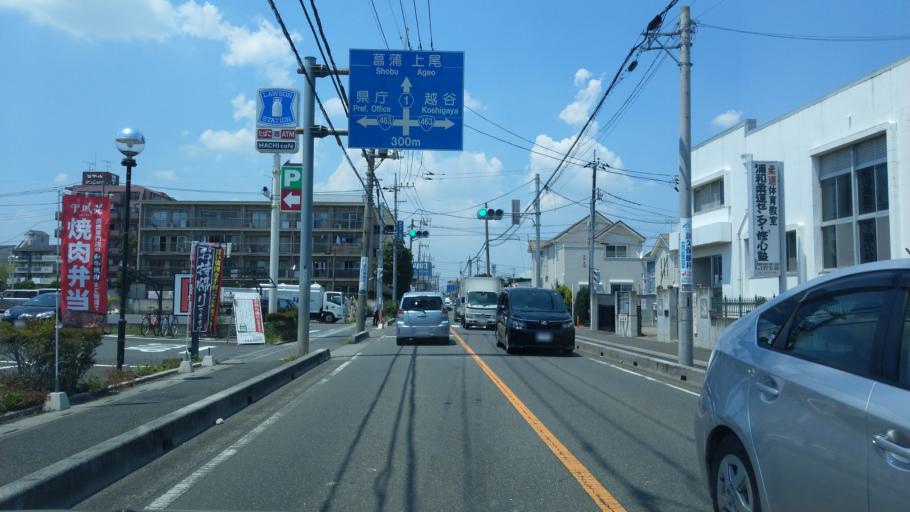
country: JP
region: Saitama
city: Saitama
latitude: 35.8695
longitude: 139.6796
